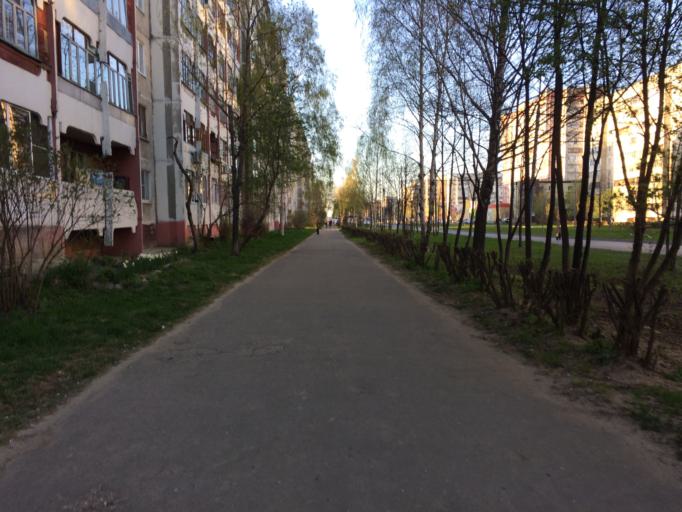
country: RU
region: Mariy-El
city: Yoshkar-Ola
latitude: 56.6280
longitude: 47.9156
